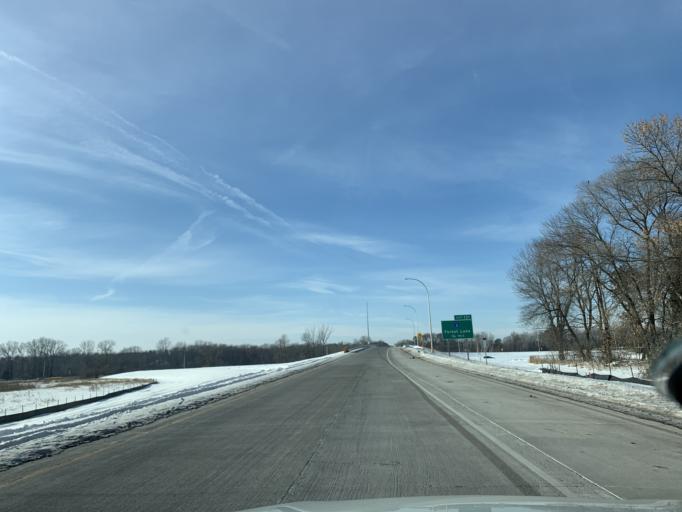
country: US
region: Minnesota
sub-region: Washington County
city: Forest Lake
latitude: 45.2899
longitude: -92.9999
